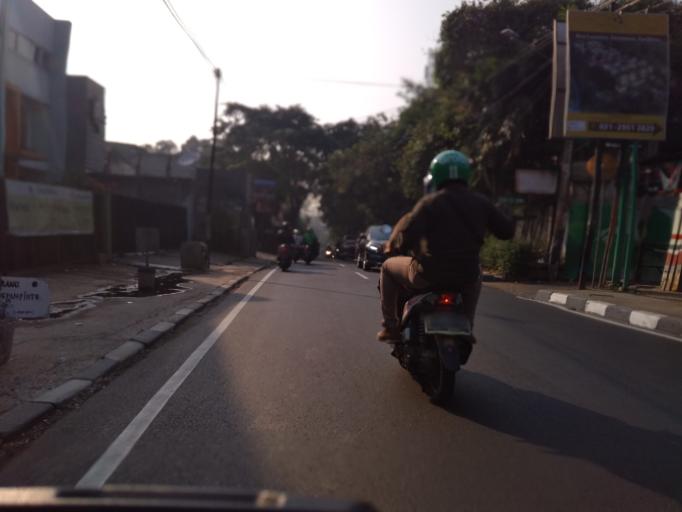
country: ID
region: Jakarta Raya
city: Jakarta
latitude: -6.2783
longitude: 106.8105
